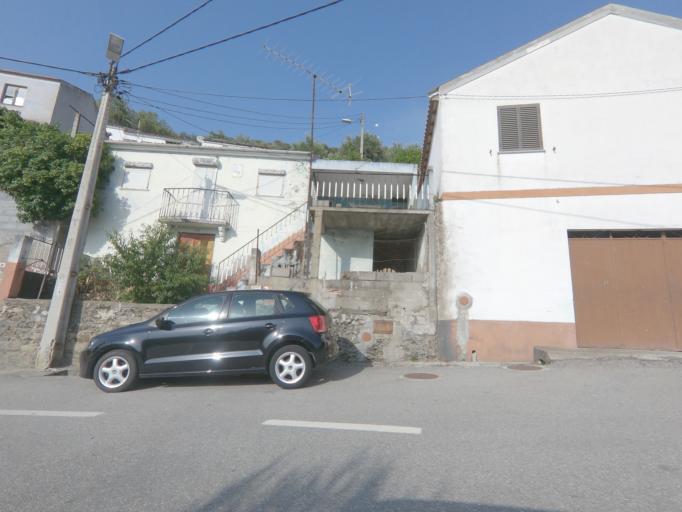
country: PT
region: Viseu
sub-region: Tabuaco
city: Tabuaco
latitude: 41.1328
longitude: -7.5330
